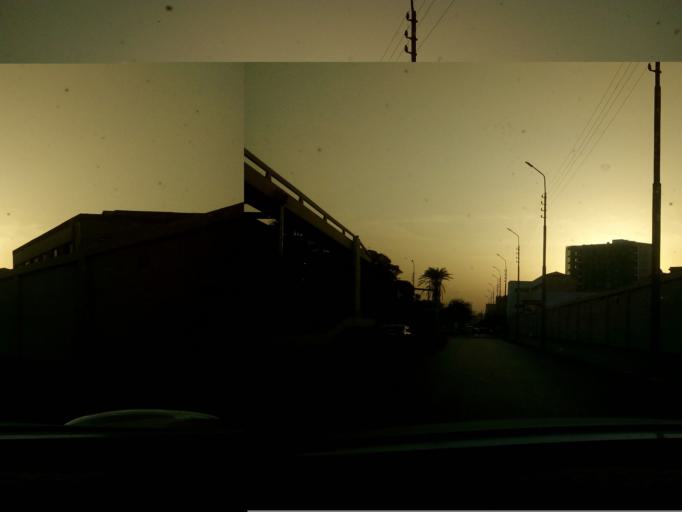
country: EG
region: Muhafazat al Qahirah
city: Cairo
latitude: 30.0922
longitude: 31.3438
